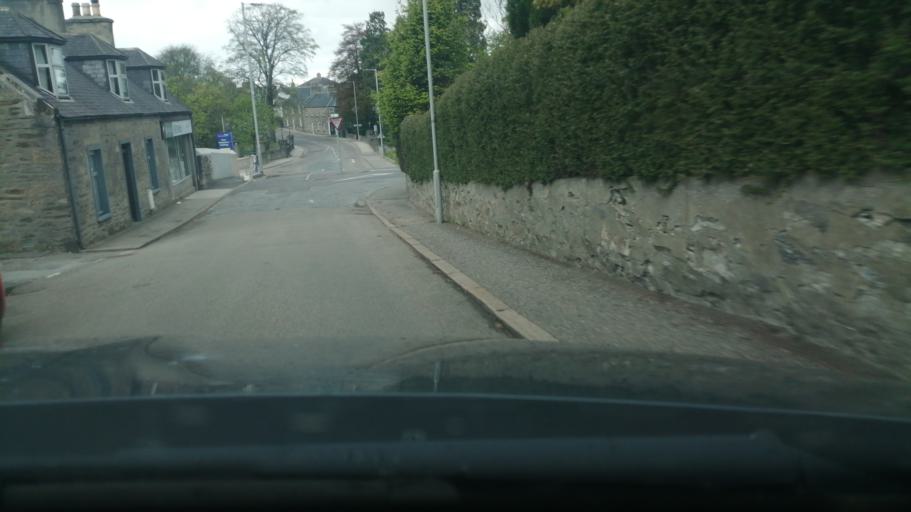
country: GB
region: Scotland
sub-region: Moray
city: Keith
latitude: 57.5429
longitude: -2.9558
